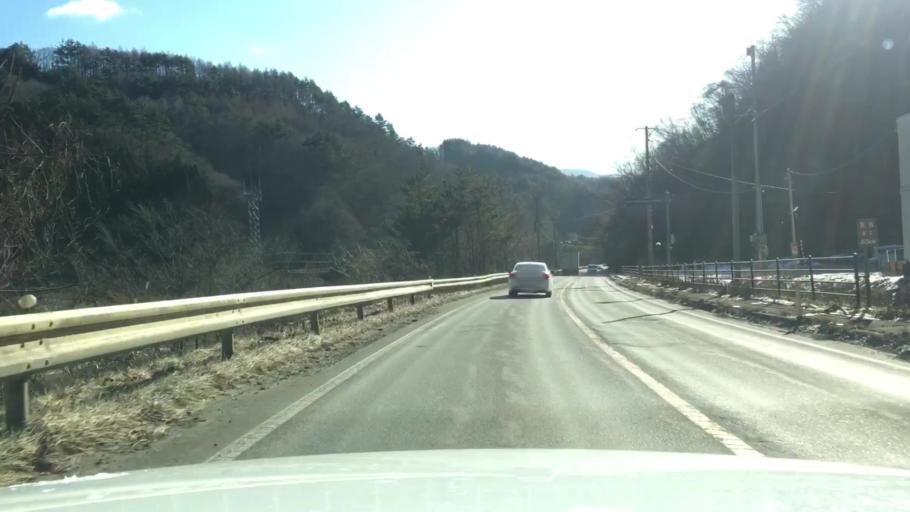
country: JP
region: Iwate
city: Tono
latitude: 39.6214
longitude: 141.6197
